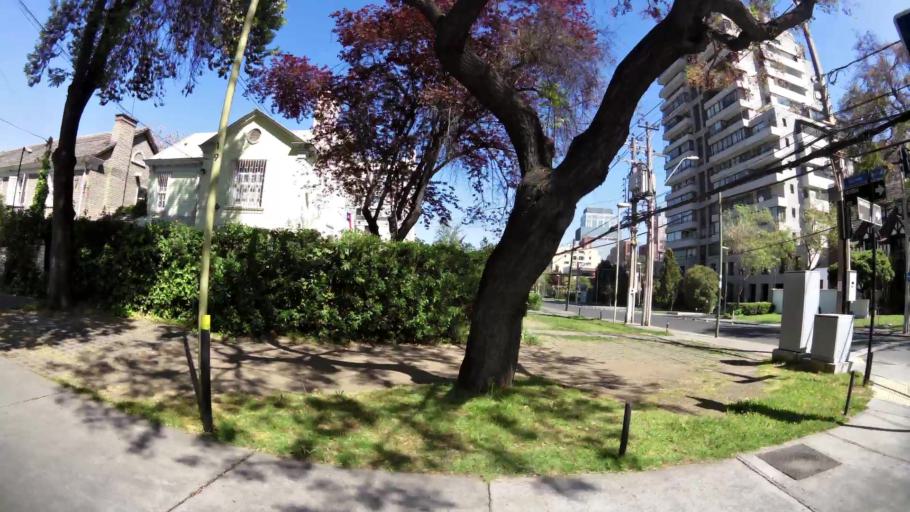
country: CL
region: Santiago Metropolitan
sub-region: Provincia de Santiago
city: Villa Presidente Frei, Nunoa, Santiago, Chile
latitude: -33.4146
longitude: -70.5803
